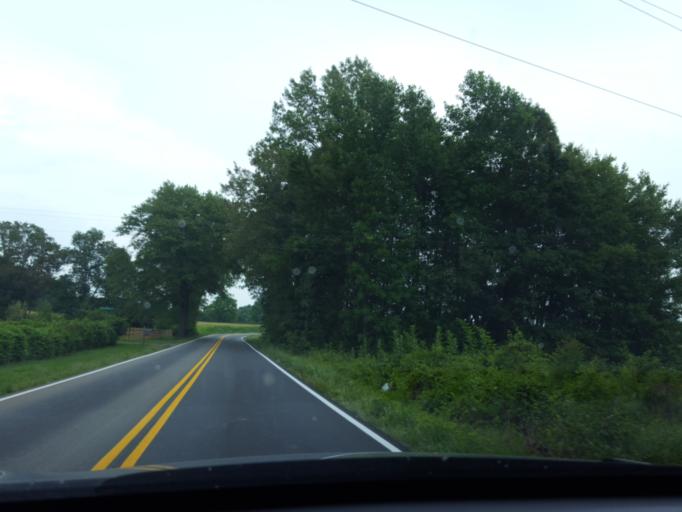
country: US
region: Virginia
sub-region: Spotsylvania County
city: Spotsylvania
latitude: 38.2624
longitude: -77.8224
